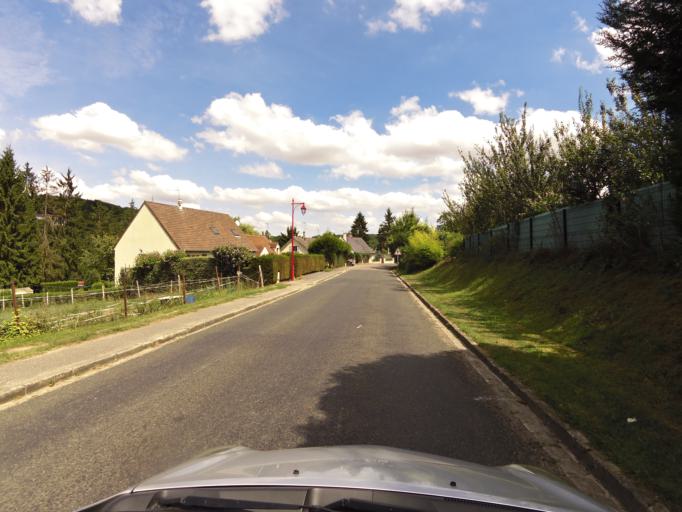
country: FR
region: Picardie
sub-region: Departement de l'Aisne
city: Neuilly-Saint-Front
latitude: 49.2521
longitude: 3.2076
